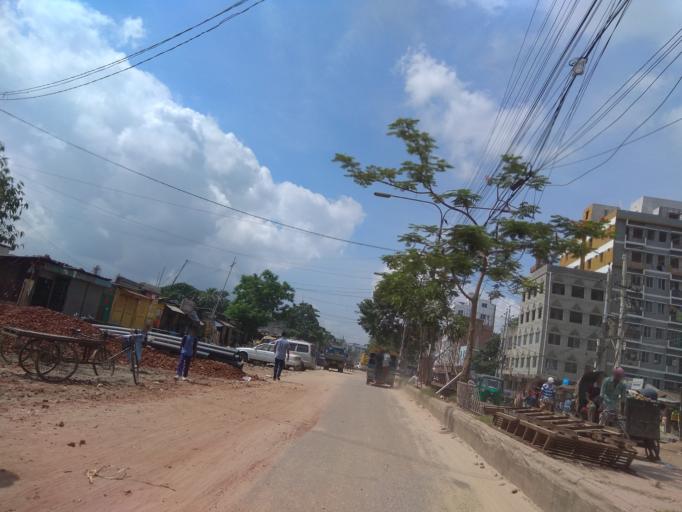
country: BD
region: Dhaka
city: Paltan
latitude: 23.8022
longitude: 90.3880
